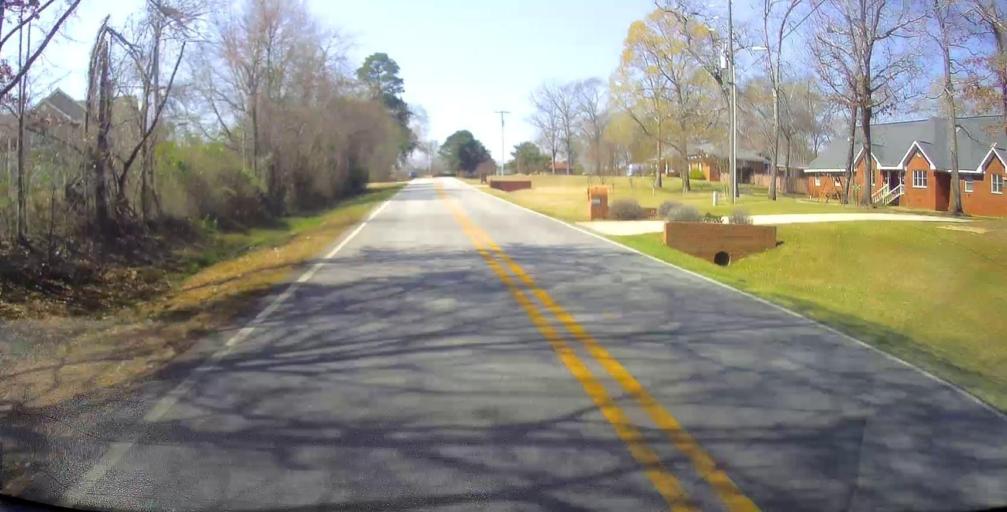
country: US
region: Georgia
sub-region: Houston County
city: Centerville
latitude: 32.5952
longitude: -83.7124
